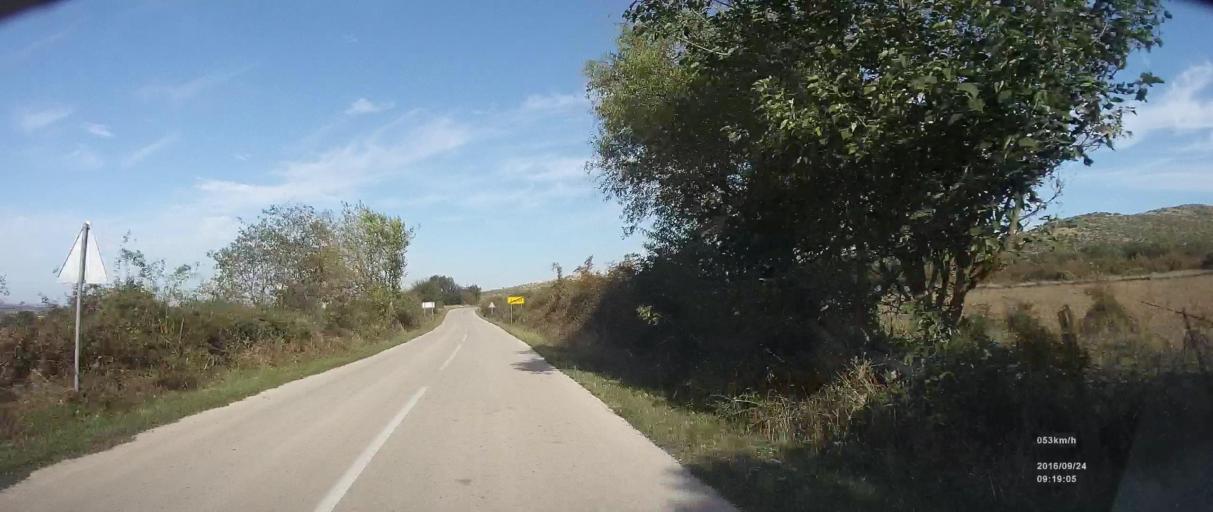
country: HR
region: Zadarska
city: Polaca
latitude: 44.0599
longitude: 15.5072
